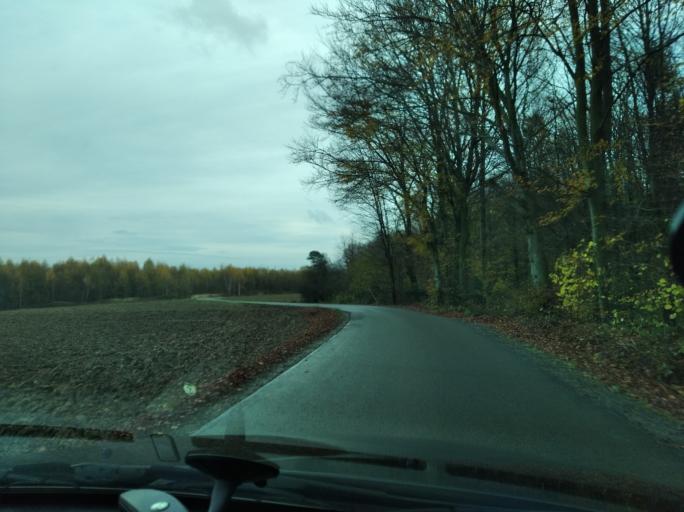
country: PL
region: Subcarpathian Voivodeship
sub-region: Powiat strzyzowski
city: Strzyzow
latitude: 49.9092
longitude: 21.7753
